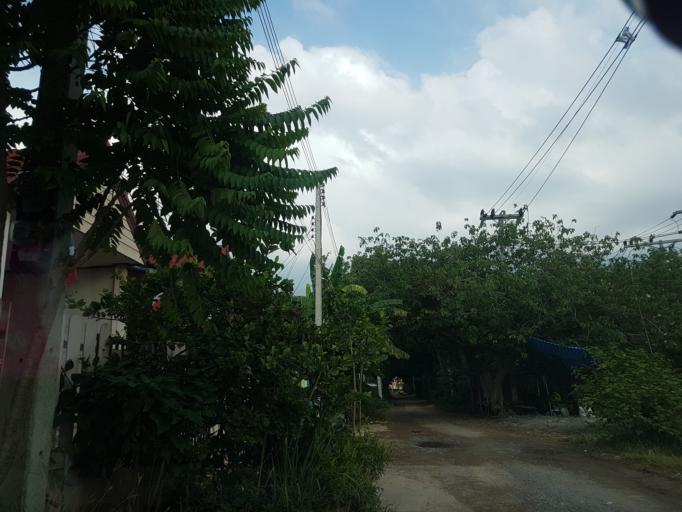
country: TH
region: Lop Buri
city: Lop Buri
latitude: 14.7683
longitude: 100.6978
